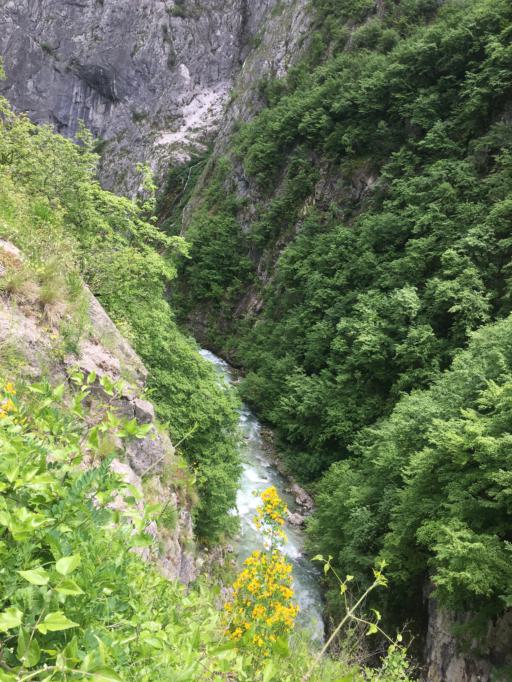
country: XK
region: Pec
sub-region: Komuna e Pejes
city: Peje
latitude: 42.6628
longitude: 20.2172
